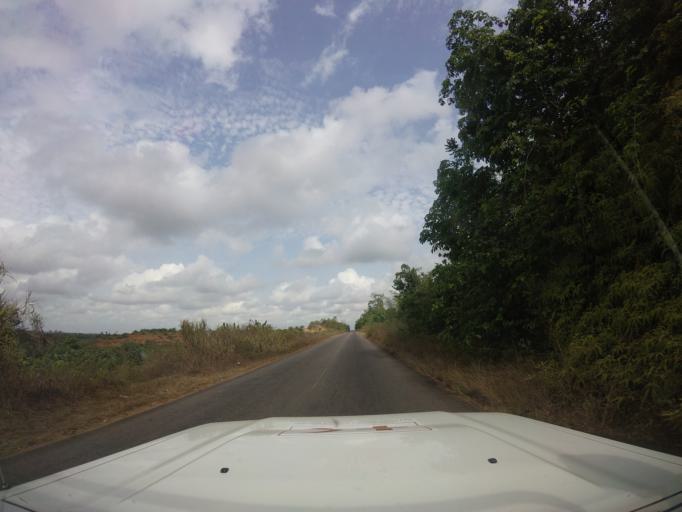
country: LR
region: Bomi
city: Tubmanburg
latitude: 6.7096
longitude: -10.9318
